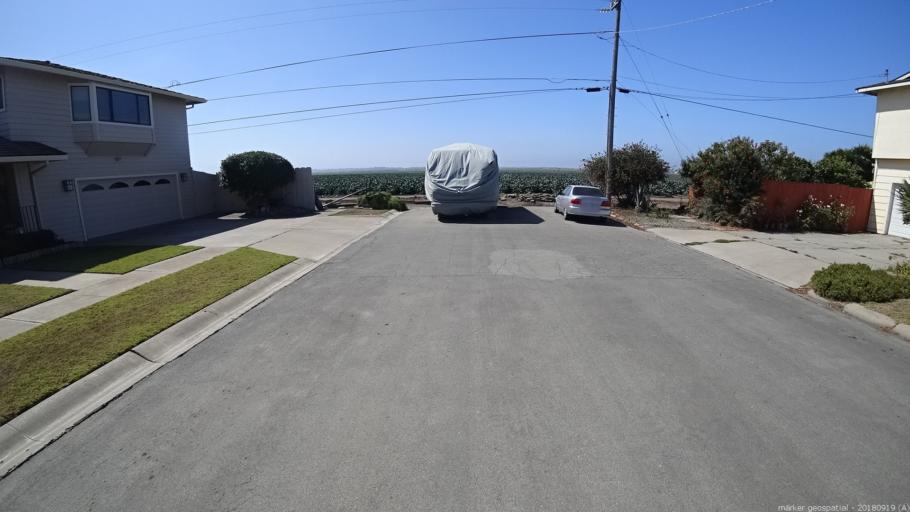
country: US
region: California
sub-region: Monterey County
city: Castroville
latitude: 36.7582
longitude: -121.7498
